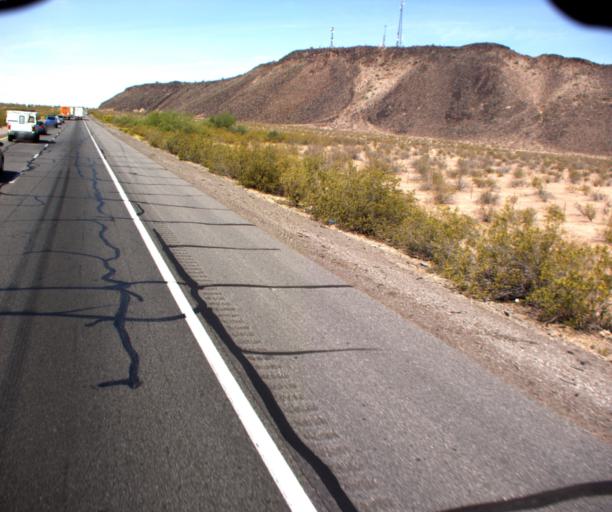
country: US
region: Arizona
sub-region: Maricopa County
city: Buckeye
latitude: 33.5261
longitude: -113.1004
